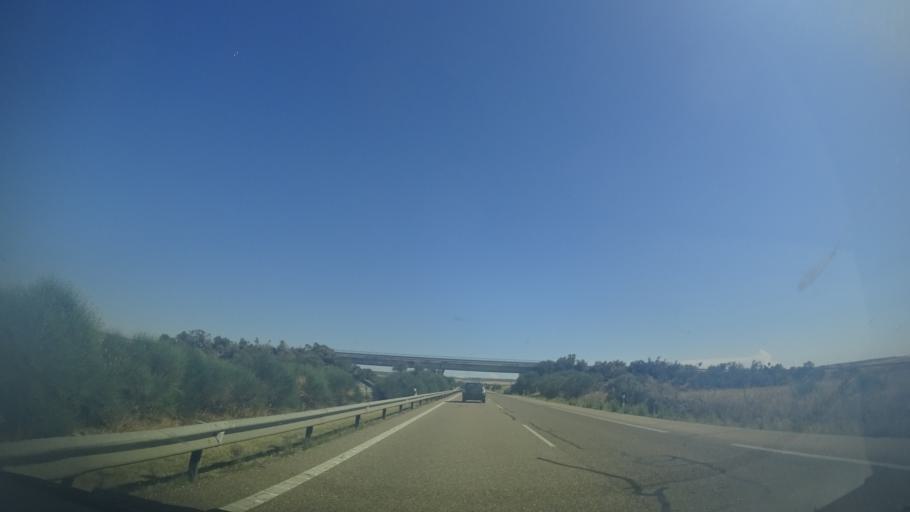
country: ES
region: Castille and Leon
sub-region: Provincia de Valladolid
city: Villanueva de los Caballeros
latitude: 41.7500
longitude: -5.2808
